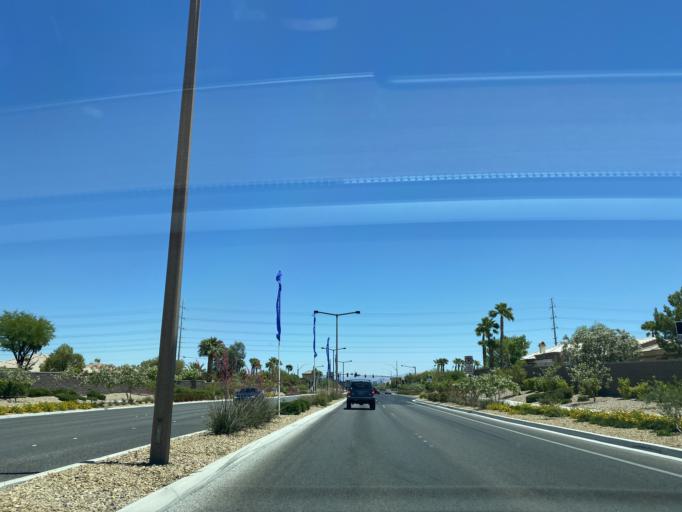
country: US
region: Nevada
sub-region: Clark County
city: Summerlin South
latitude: 36.1002
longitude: -115.3177
